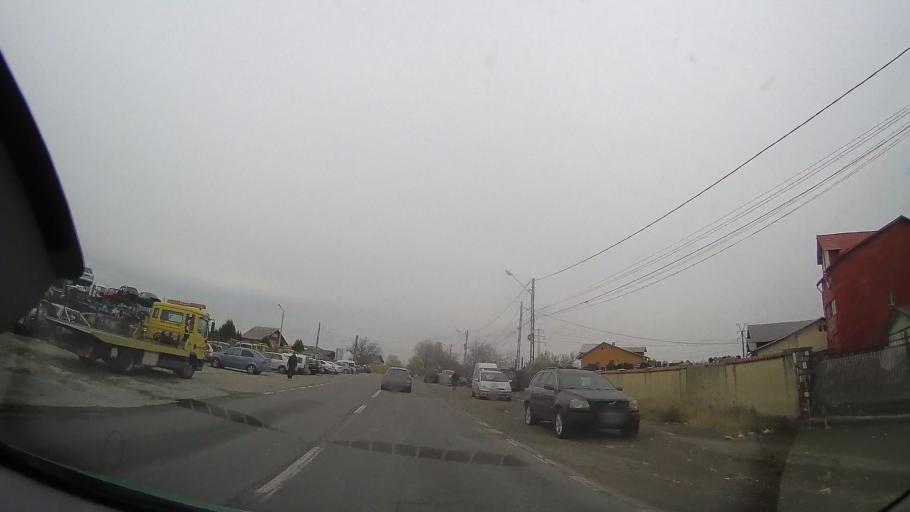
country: RO
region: Prahova
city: Ploiesti
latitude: 44.9630
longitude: 26.0373
